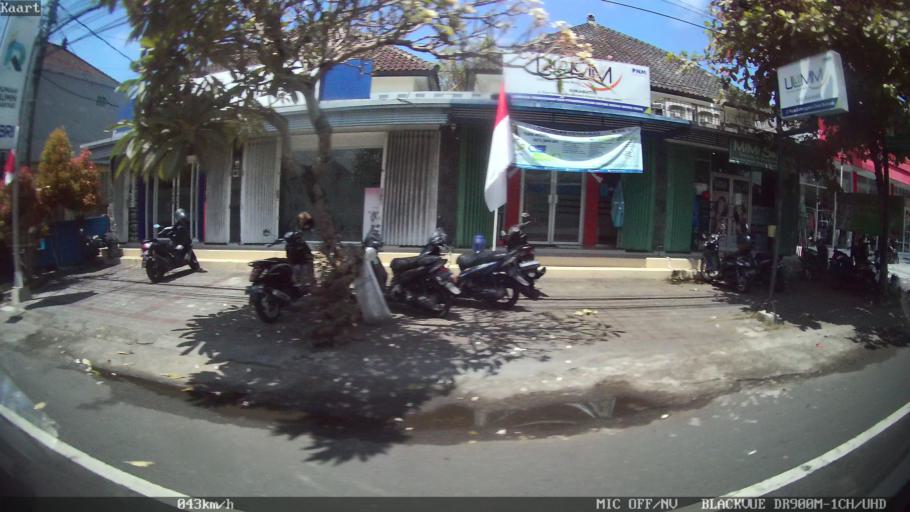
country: ID
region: Bali
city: Banjar Pasekan
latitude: -8.6031
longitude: 115.2789
